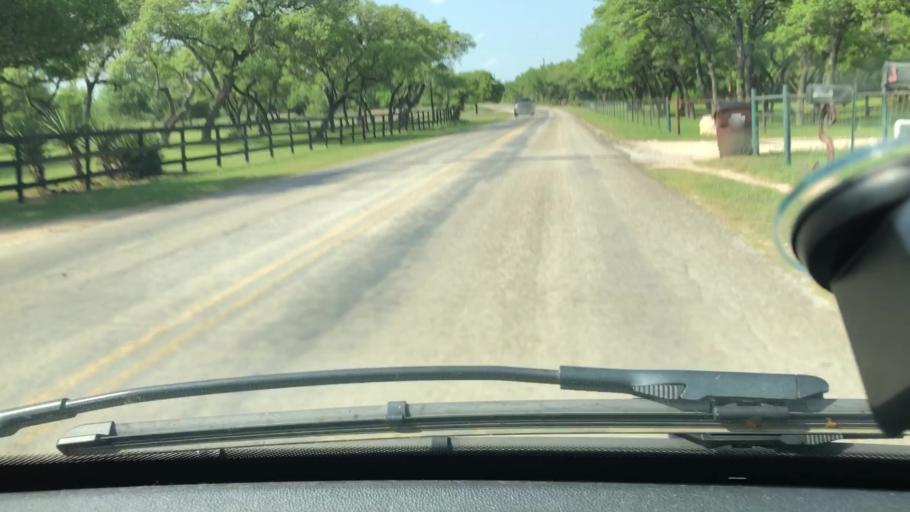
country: US
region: Texas
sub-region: Comal County
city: Bulverde
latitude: 29.7625
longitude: -98.4586
